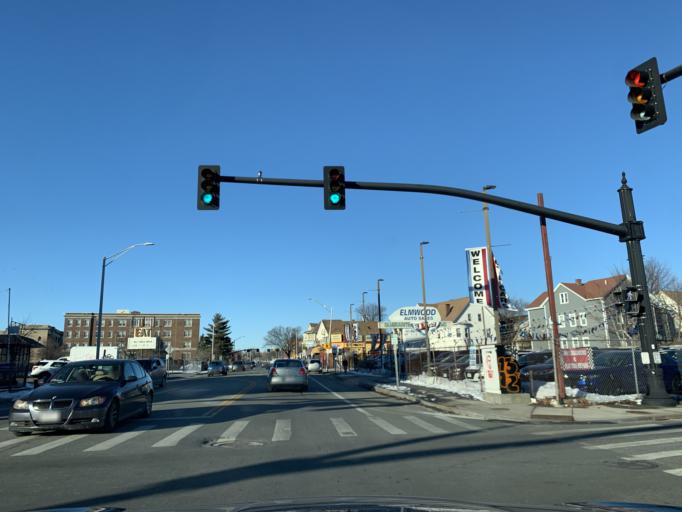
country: US
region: Rhode Island
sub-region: Providence County
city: Cranston
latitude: 41.8023
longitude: -71.4261
